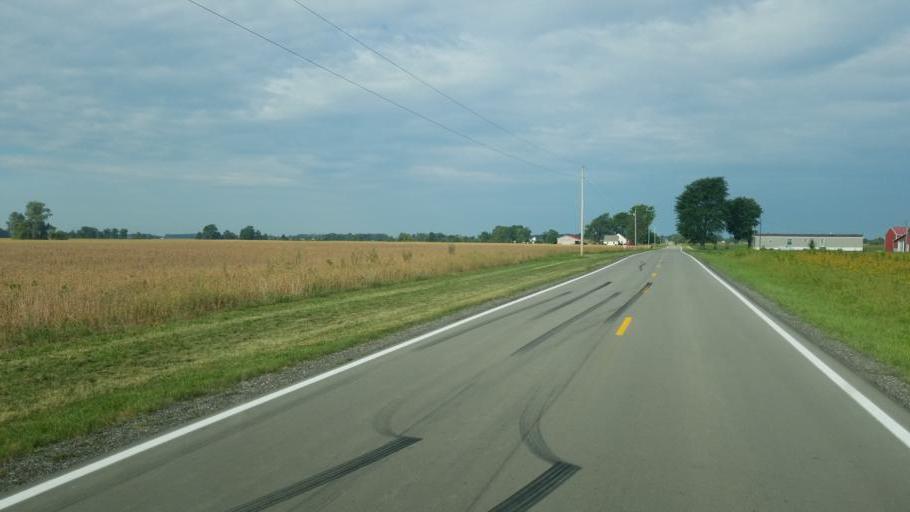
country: US
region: Ohio
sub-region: Marion County
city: Marion
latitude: 40.7174
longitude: -83.1024
